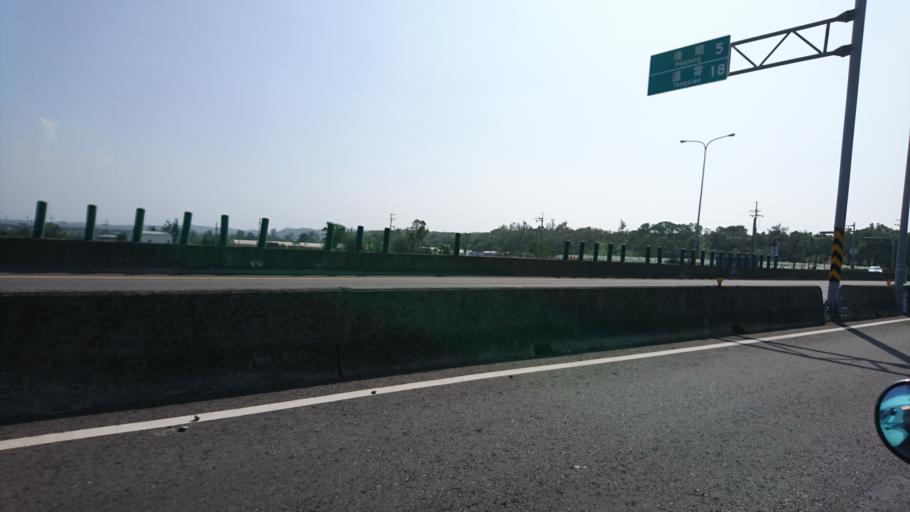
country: TW
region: Taiwan
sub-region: Miaoli
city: Miaoli
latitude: 24.6740
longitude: 120.8396
